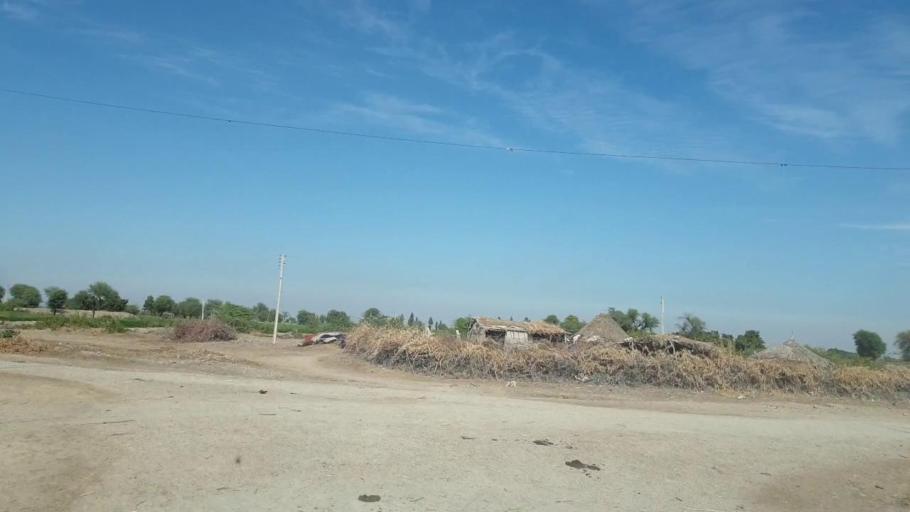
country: PK
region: Sindh
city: Pithoro
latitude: 25.6220
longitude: 69.2573
